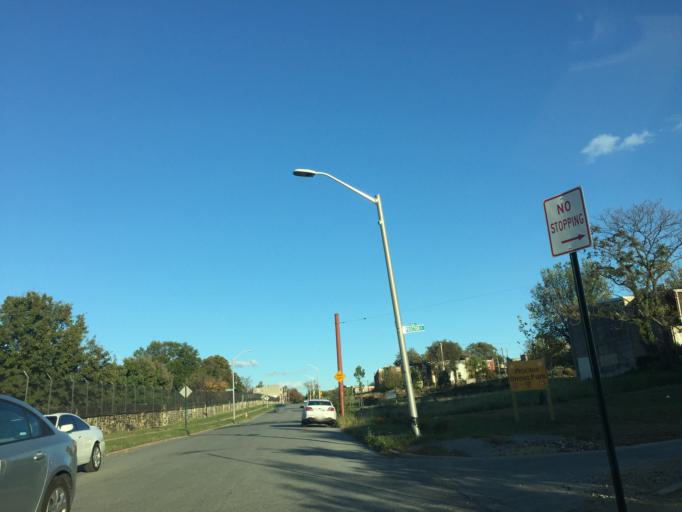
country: US
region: Maryland
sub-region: City of Baltimore
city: Baltimore
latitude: 39.3059
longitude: -76.6075
